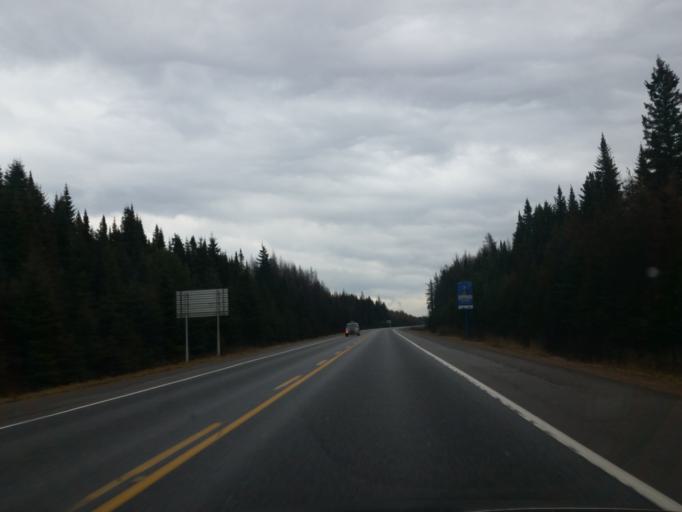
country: CA
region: Quebec
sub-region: Capitale-Nationale
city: Shannon
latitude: 46.8790
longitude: -71.4608
